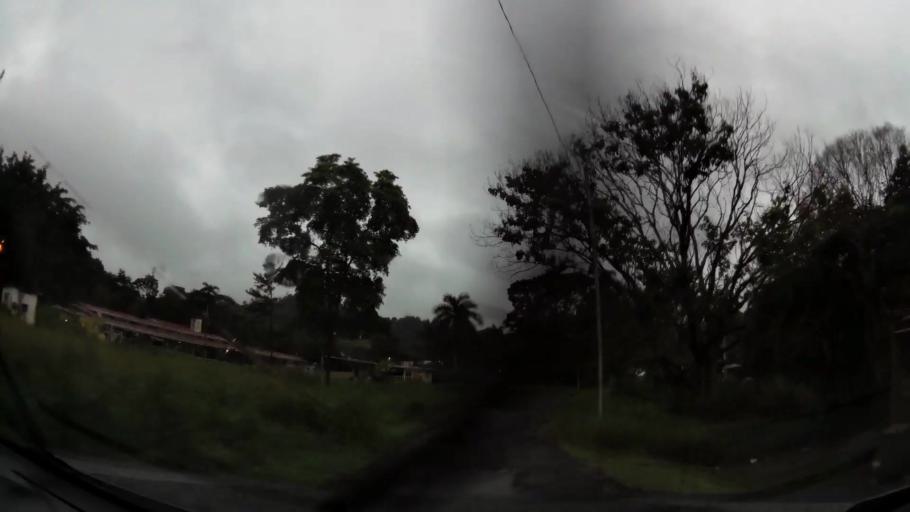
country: PA
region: Panama
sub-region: Distrito de Panama
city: Paraiso
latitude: 9.0313
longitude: -79.6271
